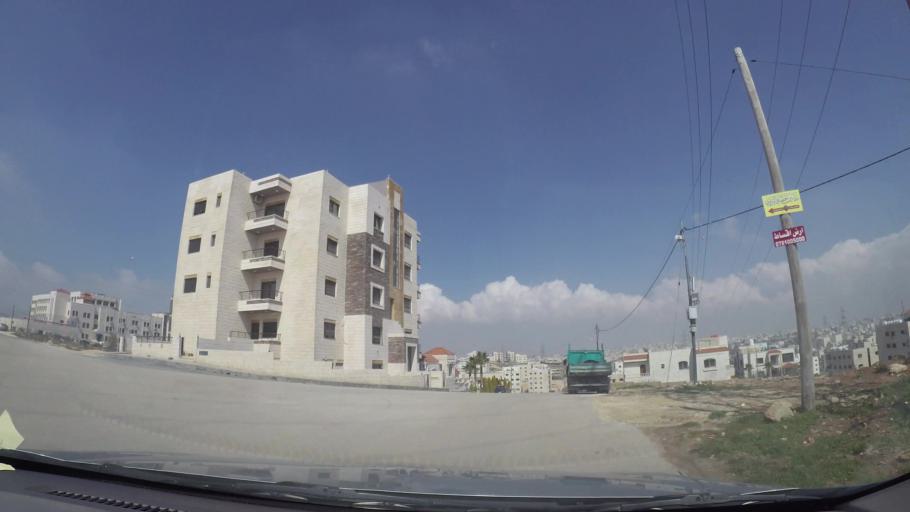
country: JO
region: Amman
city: Al Bunayyat ash Shamaliyah
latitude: 31.8884
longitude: 35.8970
